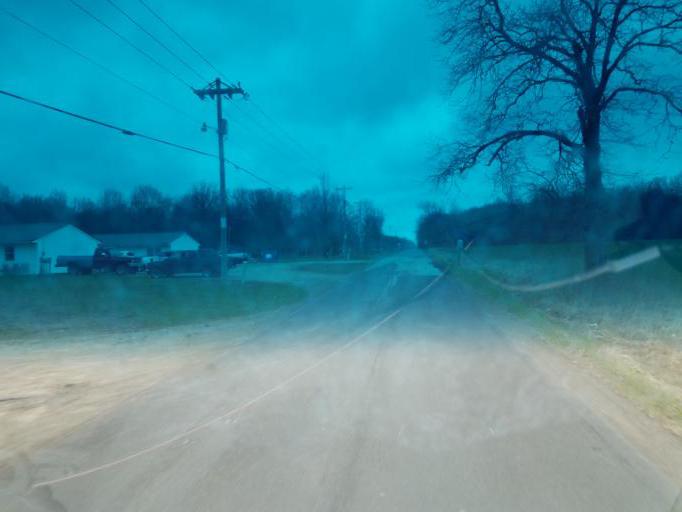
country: US
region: Ohio
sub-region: Knox County
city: Centerburg
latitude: 40.4019
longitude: -82.7885
